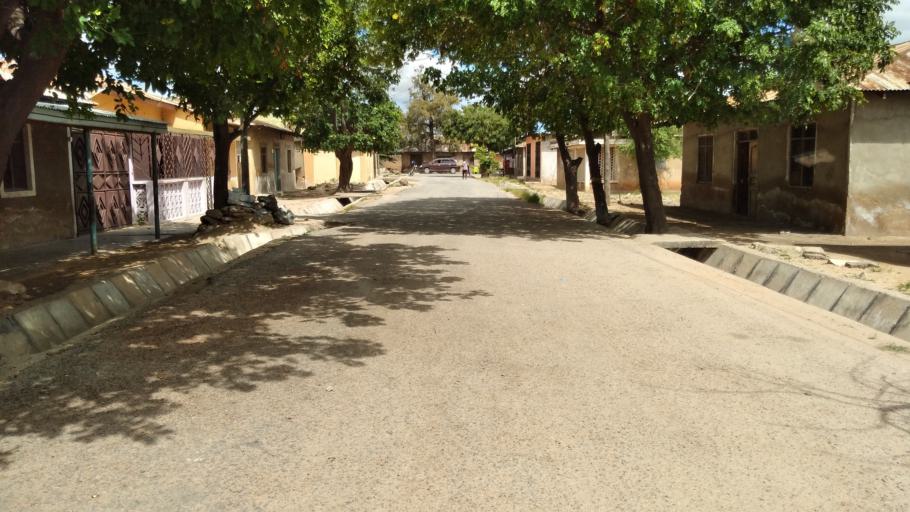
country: TZ
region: Dodoma
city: Dodoma
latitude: -6.1729
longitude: 35.7498
